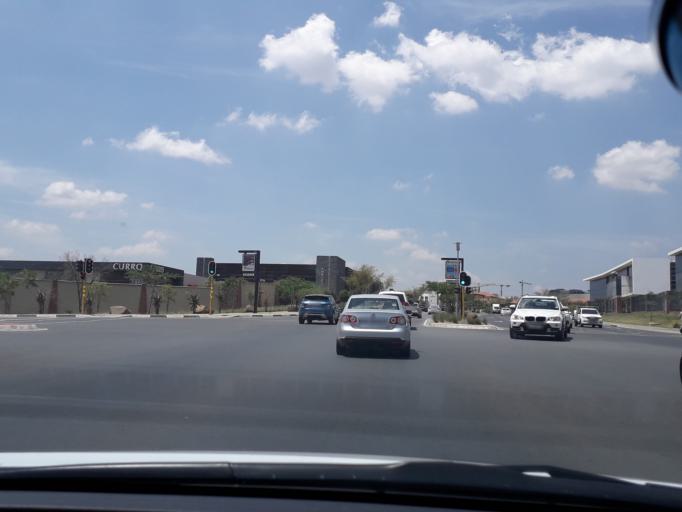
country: ZA
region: Gauteng
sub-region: City of Johannesburg Metropolitan Municipality
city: Midrand
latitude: -26.0142
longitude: 28.0957
